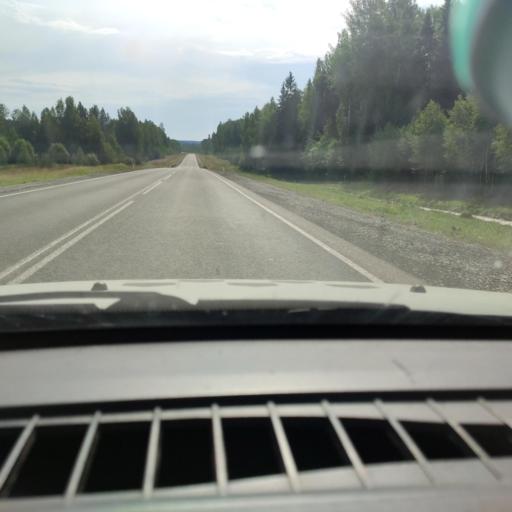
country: RU
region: Perm
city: Siva
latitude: 58.3939
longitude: 54.5261
